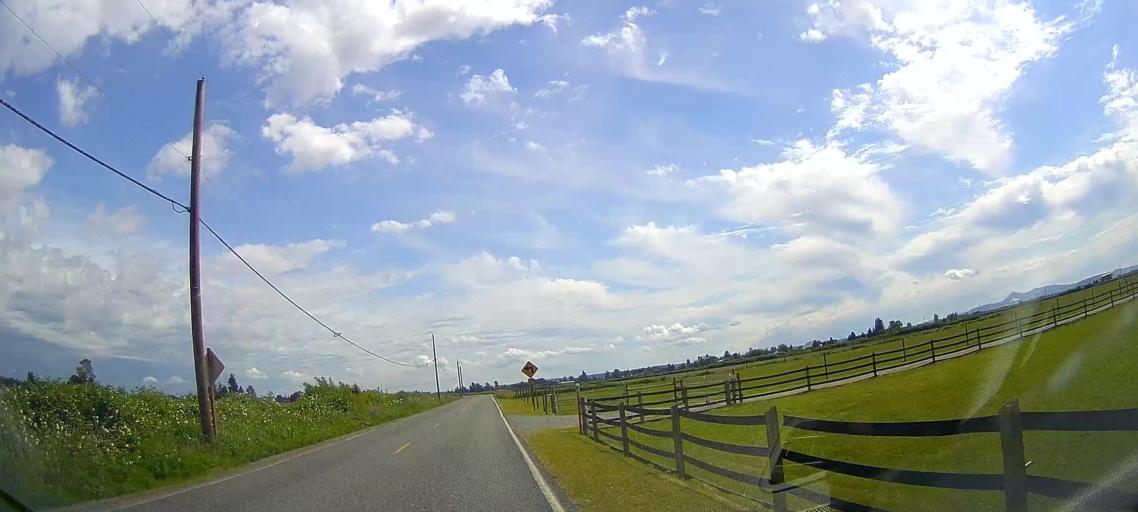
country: US
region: Washington
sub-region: Skagit County
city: Burlington
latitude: 48.5867
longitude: -122.4164
